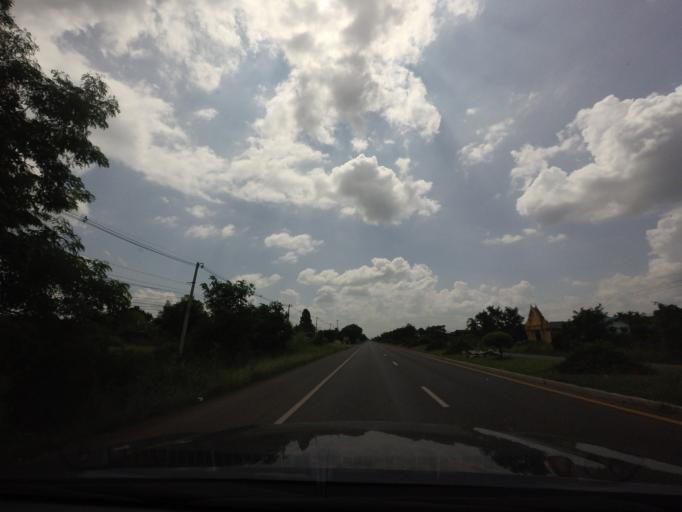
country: TH
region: Phetchabun
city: Nong Phai
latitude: 16.1721
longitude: 101.0789
